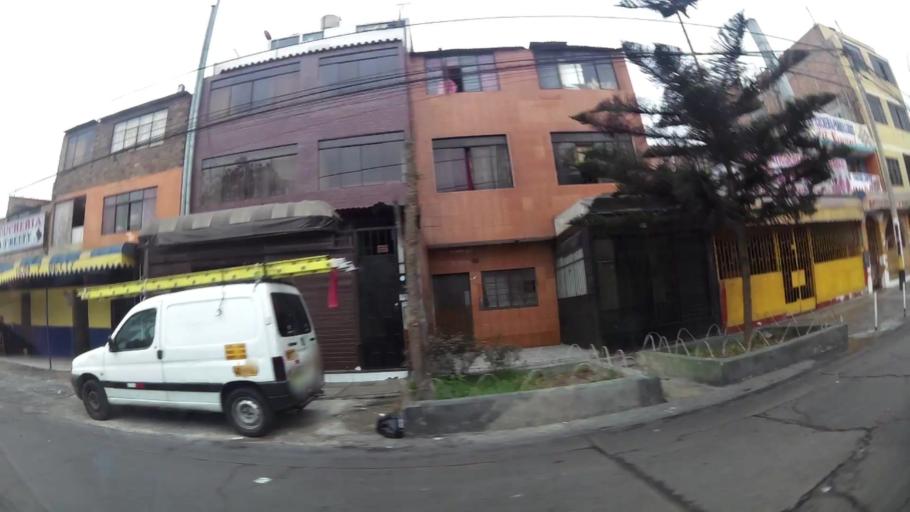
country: PE
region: Lima
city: Lima
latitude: -12.0672
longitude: -77.0597
